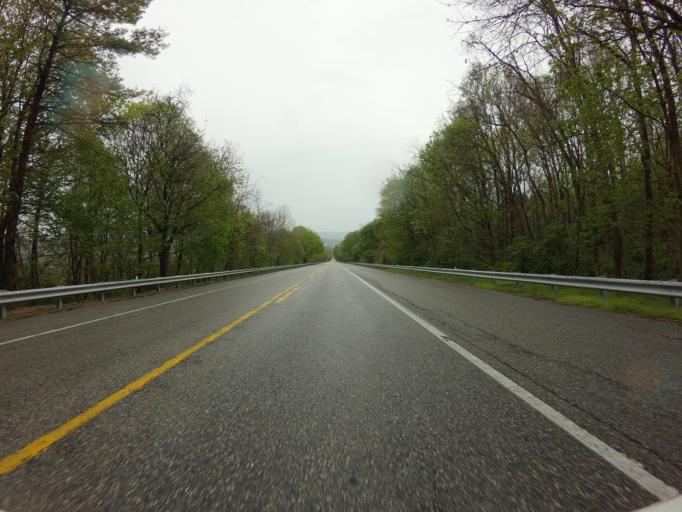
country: US
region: Maryland
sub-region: Frederick County
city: Myersville
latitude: 39.5261
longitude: -77.5845
